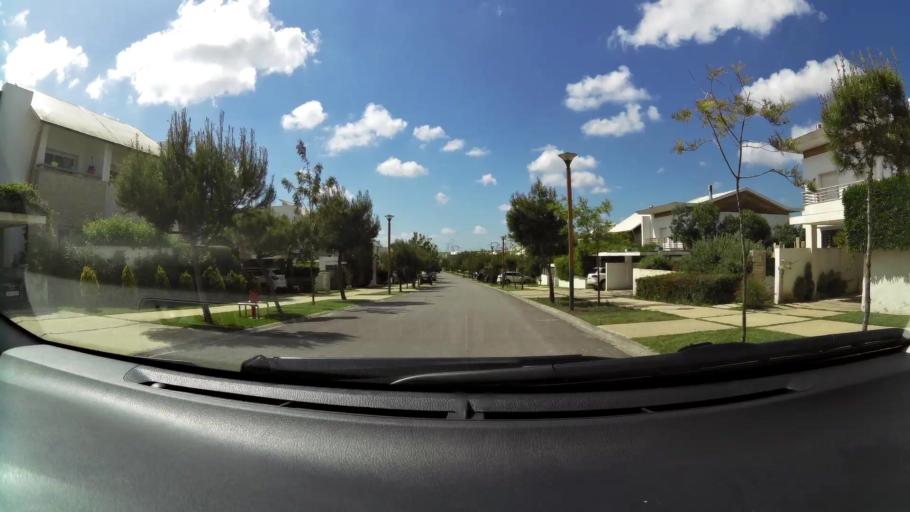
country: MA
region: Grand Casablanca
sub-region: Mediouna
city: Mediouna
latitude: 33.4903
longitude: -7.5847
